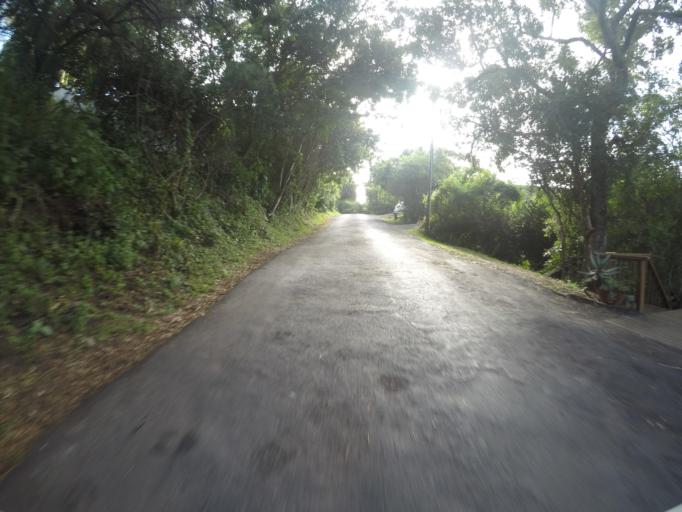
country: ZA
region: Eastern Cape
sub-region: Buffalo City Metropolitan Municipality
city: East London
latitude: -32.9681
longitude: 27.9553
